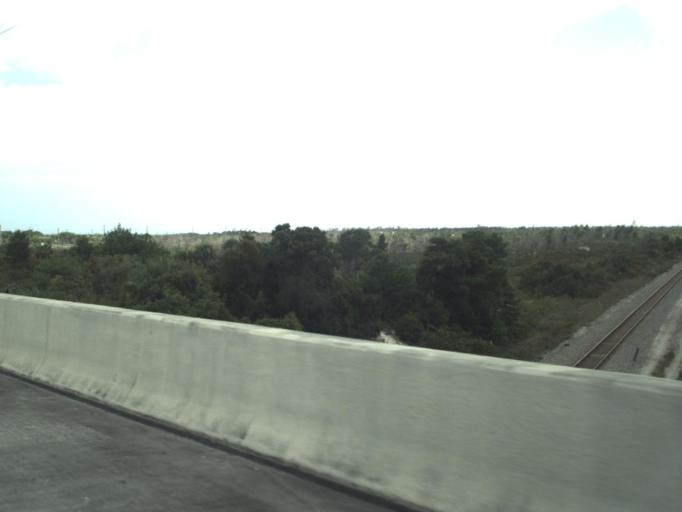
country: US
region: Florida
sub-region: Martin County
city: Hobe Sound
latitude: 27.0440
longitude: -80.1174
